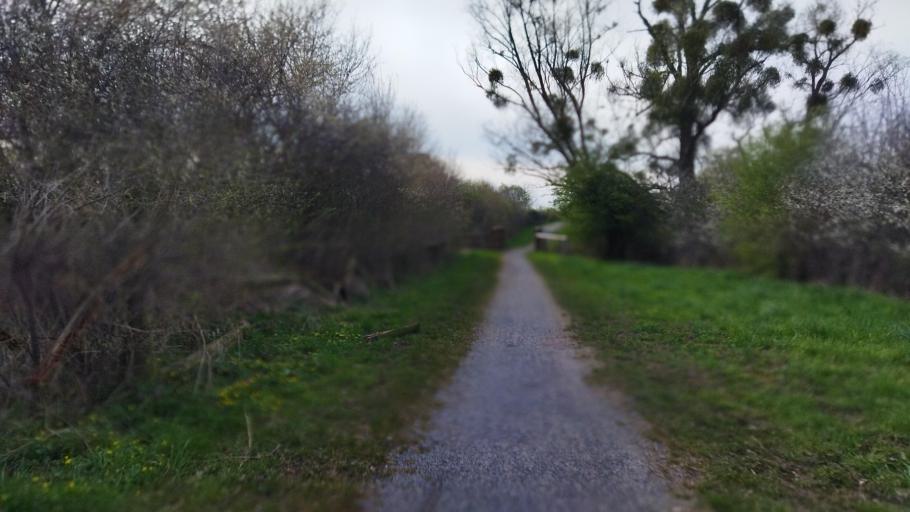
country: DE
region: Lower Saxony
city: Buchholz
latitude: 52.1919
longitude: 9.1293
